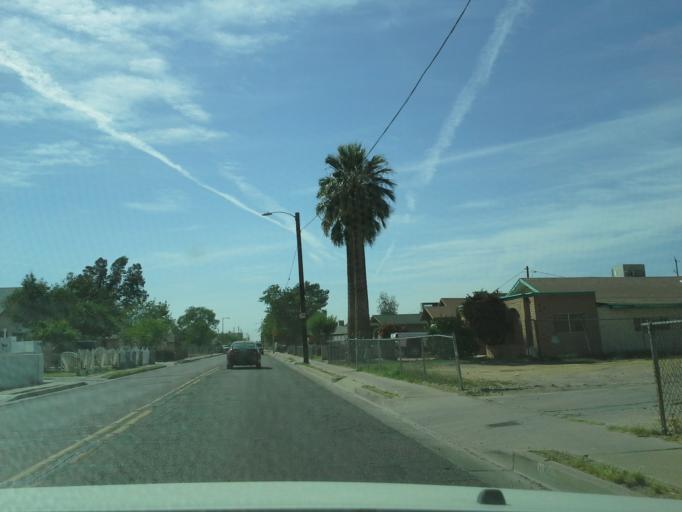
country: US
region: Arizona
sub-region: Maricopa County
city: Phoenix
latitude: 33.4587
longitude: -112.0568
